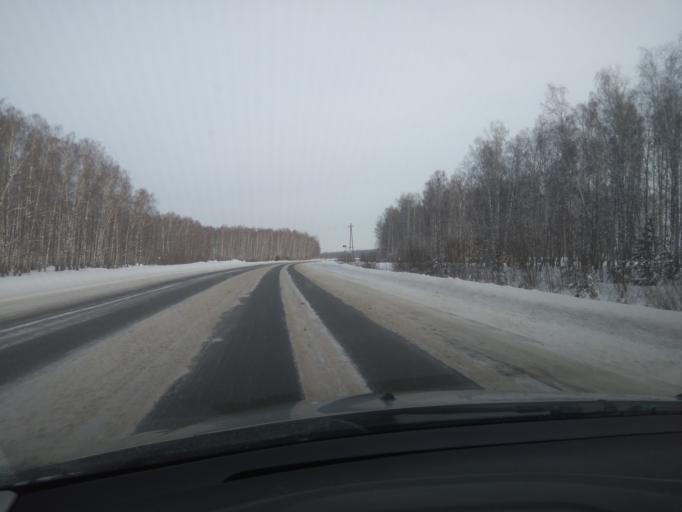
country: RU
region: Sverdlovsk
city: Bogdanovich
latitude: 56.7931
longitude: 62.0019
